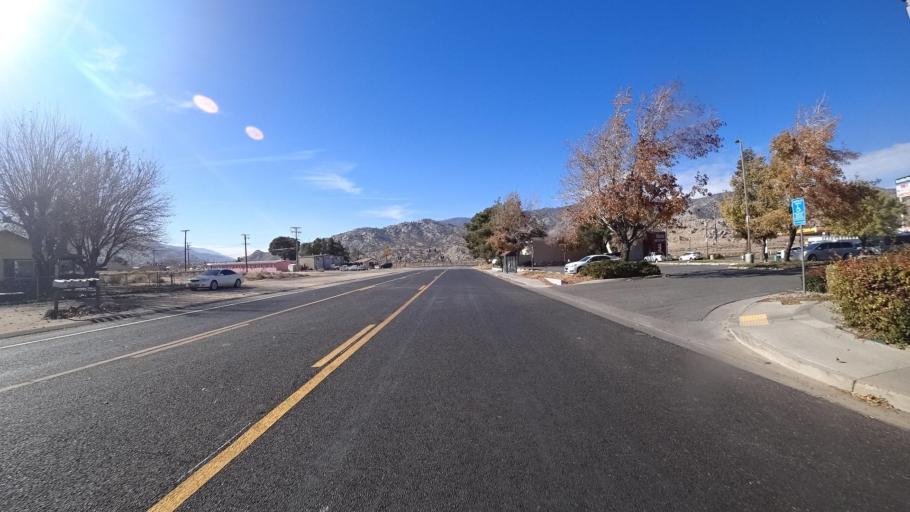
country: US
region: California
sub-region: Kern County
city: Lake Isabella
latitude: 35.6165
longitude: -118.4768
